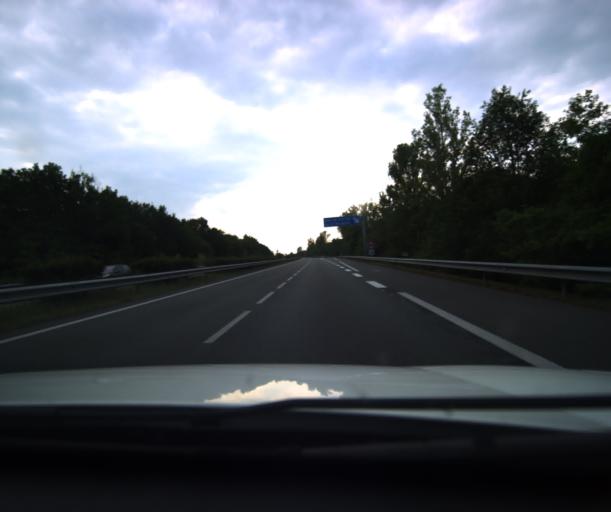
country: FR
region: Midi-Pyrenees
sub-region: Departement du Tarn-et-Garonne
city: Saint-Porquier
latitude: 44.0120
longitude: 1.2090
